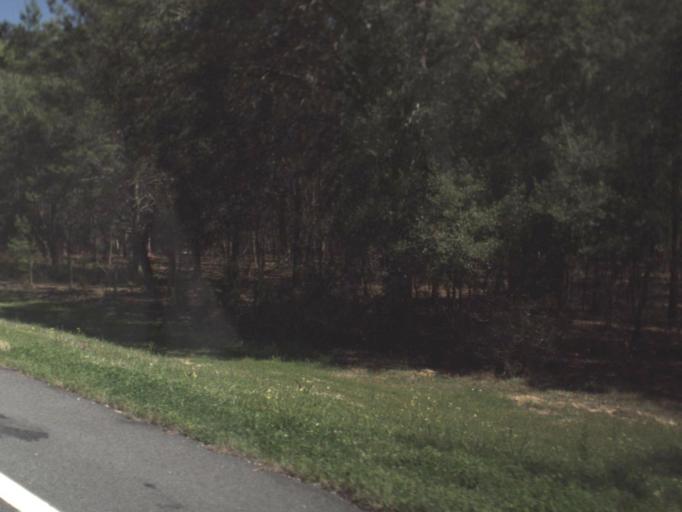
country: US
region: Florida
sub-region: Gadsden County
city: Quincy
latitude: 30.4371
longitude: -84.6473
